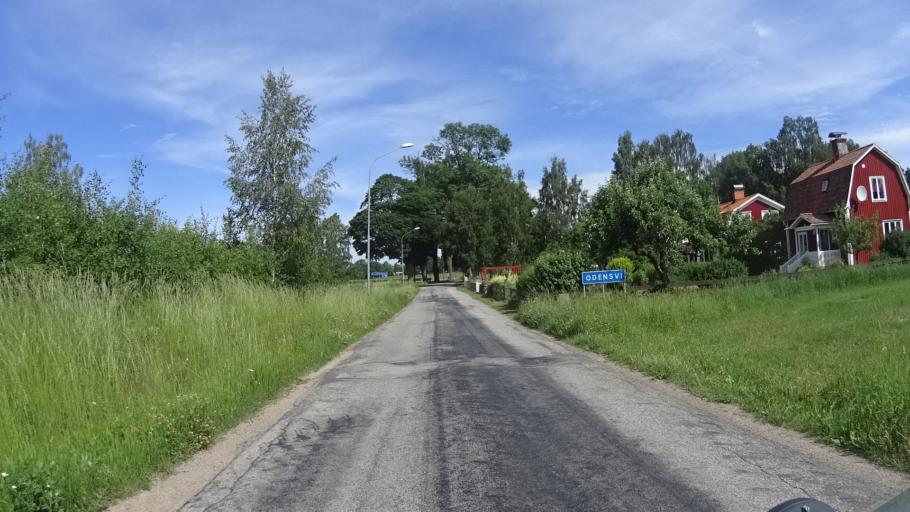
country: SE
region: Kalmar
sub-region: Vasterviks Kommun
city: Overum
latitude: 57.8904
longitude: 16.1703
